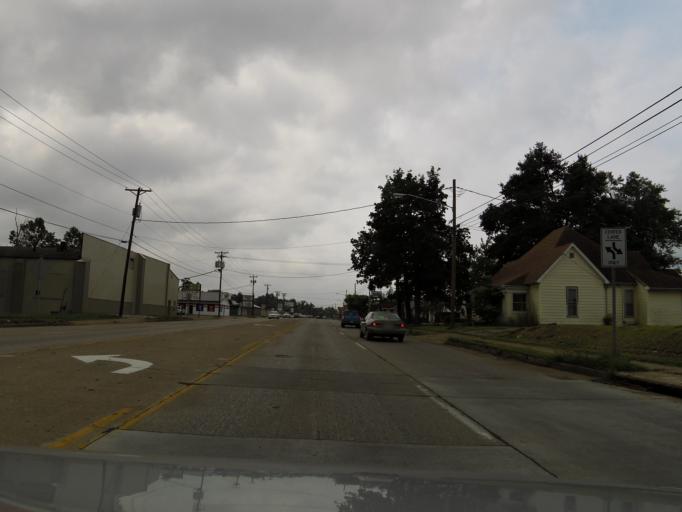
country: US
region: Kentucky
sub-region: Hopkins County
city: Madisonville
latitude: 37.3207
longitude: -87.5001
